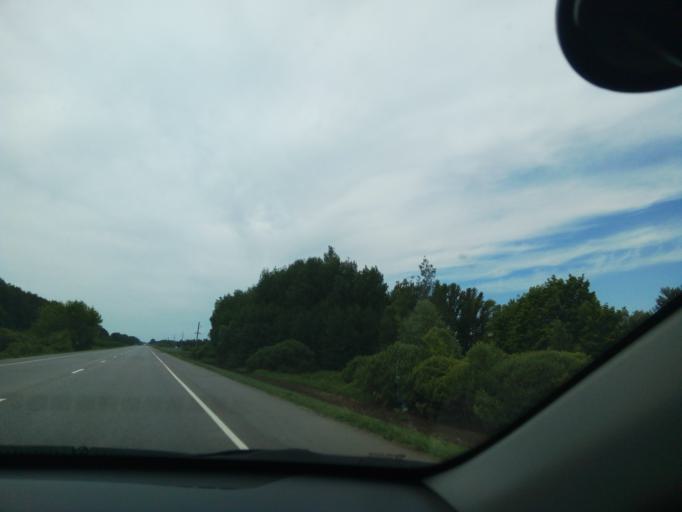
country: RU
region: Tambov
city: Selezni
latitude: 52.6761
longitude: 41.1376
